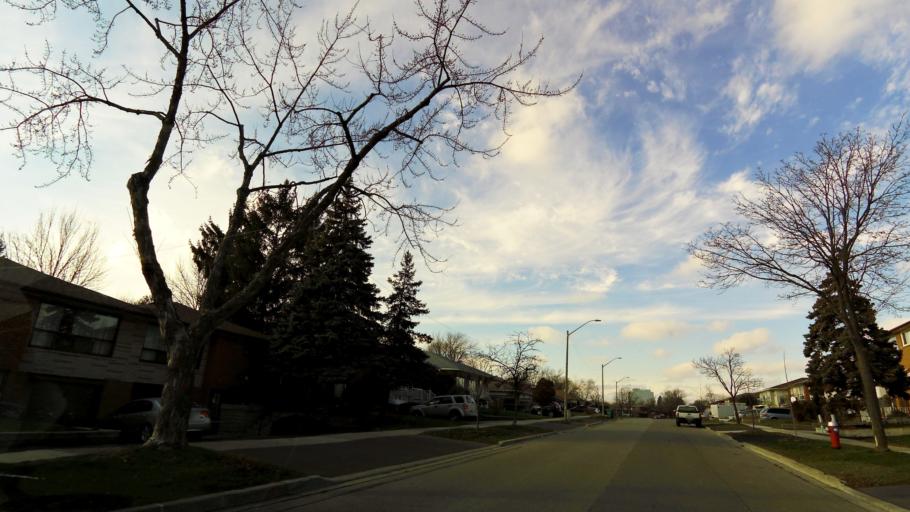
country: CA
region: Ontario
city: Mississauga
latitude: 43.5607
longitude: -79.6563
